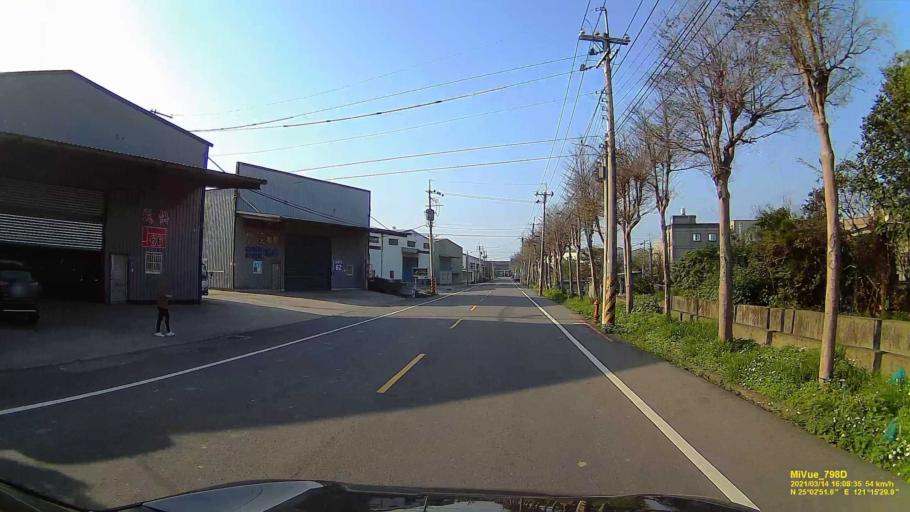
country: TW
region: Taiwan
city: Taoyuan City
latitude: 25.0478
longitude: 121.2582
